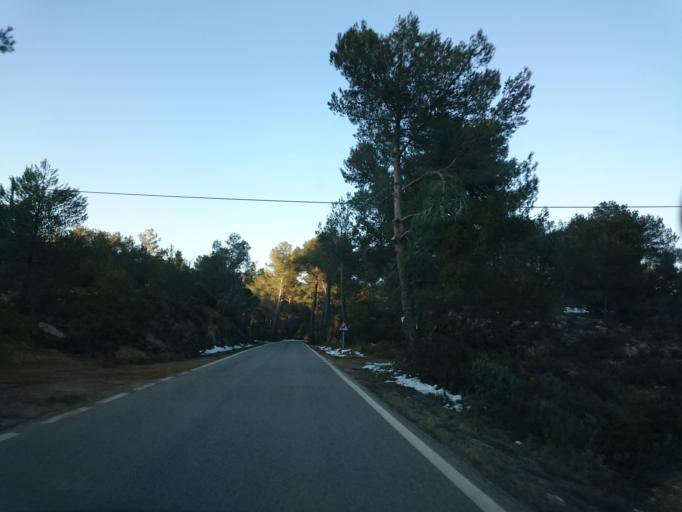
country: ES
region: Catalonia
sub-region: Provincia de Tarragona
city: la Bisbal del Penedes
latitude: 41.3625
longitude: 1.5024
